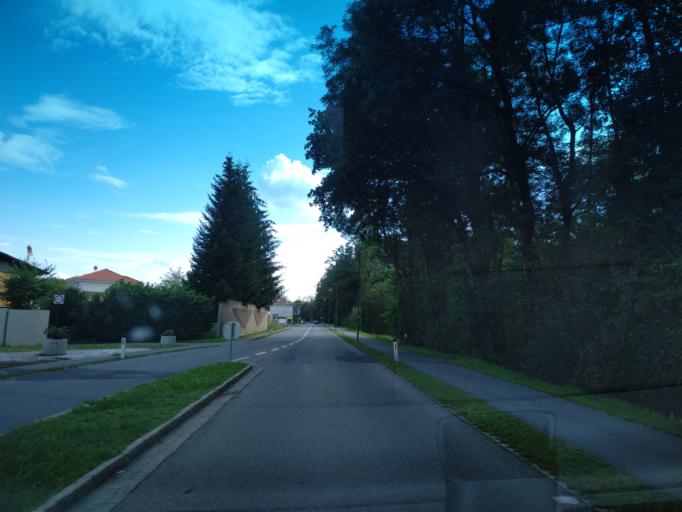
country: AT
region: Styria
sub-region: Politischer Bezirk Leibnitz
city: Kaindorf an der Sulm
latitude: 46.7887
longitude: 15.5337
